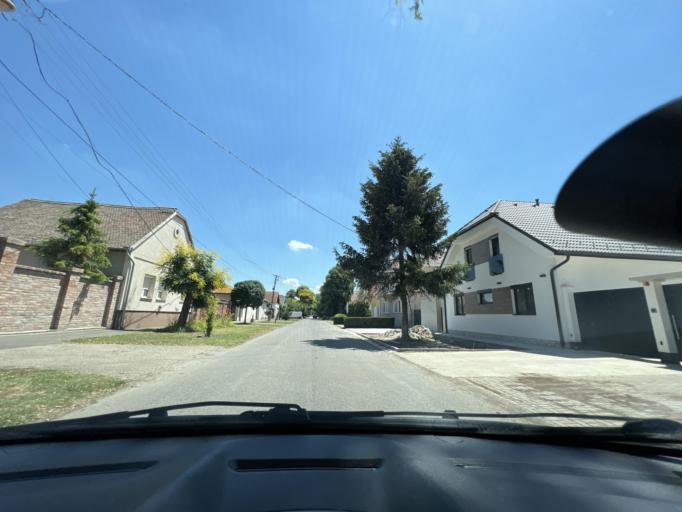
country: HU
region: Csongrad
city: Szeged
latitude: 46.2456
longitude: 20.1278
